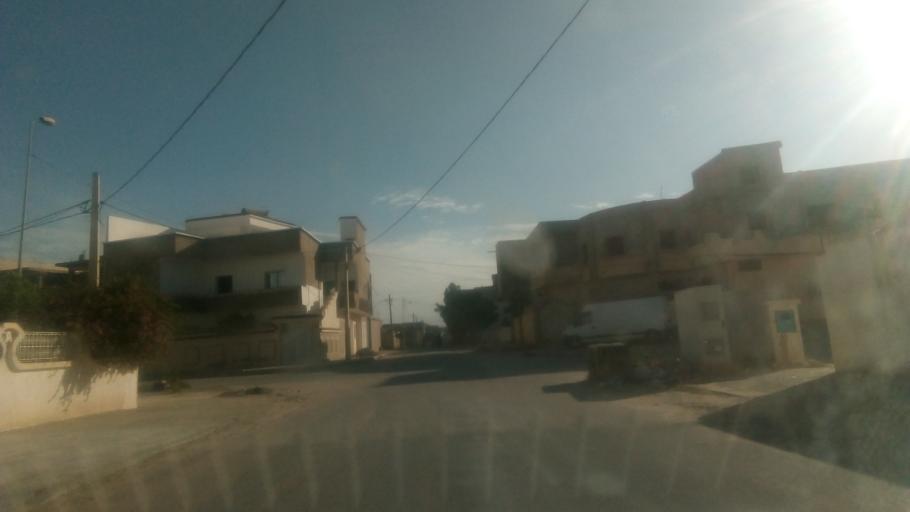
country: TN
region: Al Qayrawan
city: Kairouan
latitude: 35.6658
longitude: 10.0788
